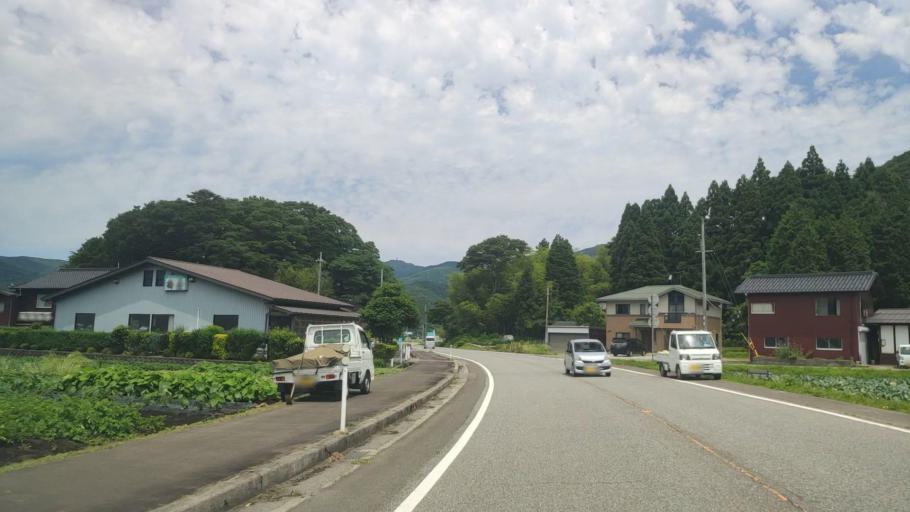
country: JP
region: Hyogo
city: Toyooka
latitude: 35.5018
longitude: 134.6725
